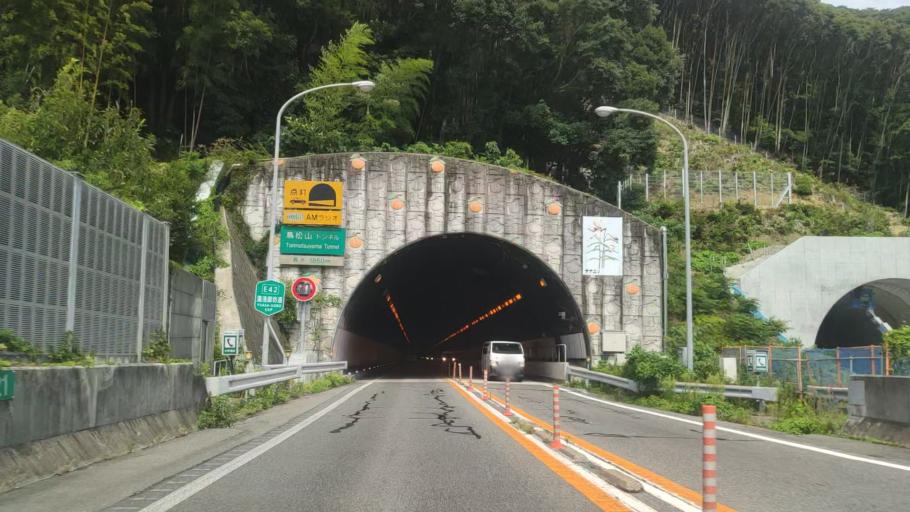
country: JP
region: Wakayama
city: Gobo
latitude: 33.9716
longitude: 135.1975
